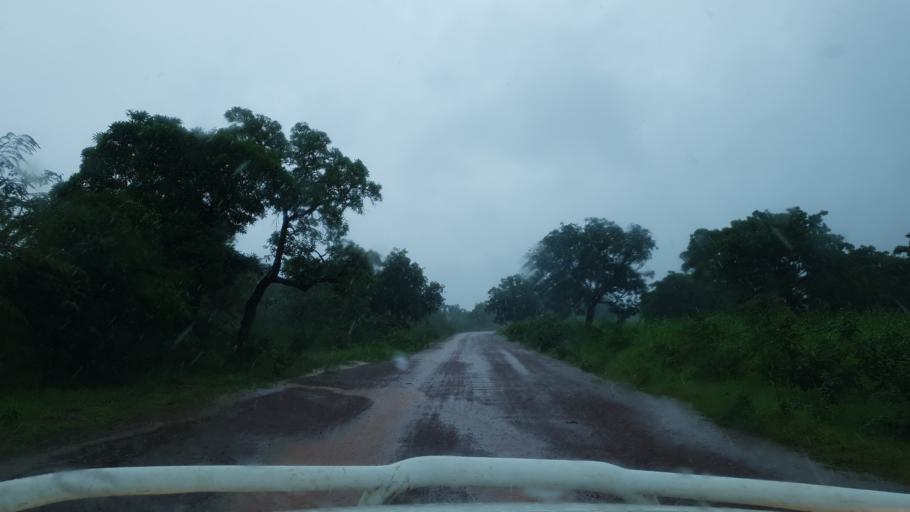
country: ML
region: Sikasso
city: Kolondieba
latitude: 11.6104
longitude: -6.6756
